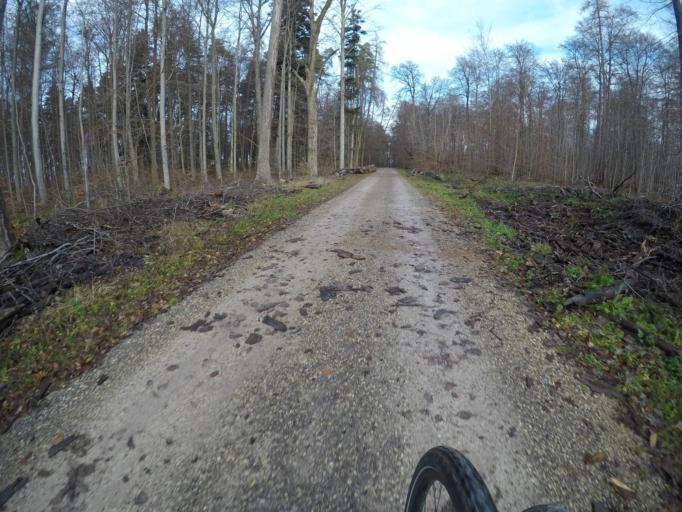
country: DE
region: Baden-Wuerttemberg
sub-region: Regierungsbezirk Stuttgart
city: Baltmannsweiler
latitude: 48.7490
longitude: 9.4276
